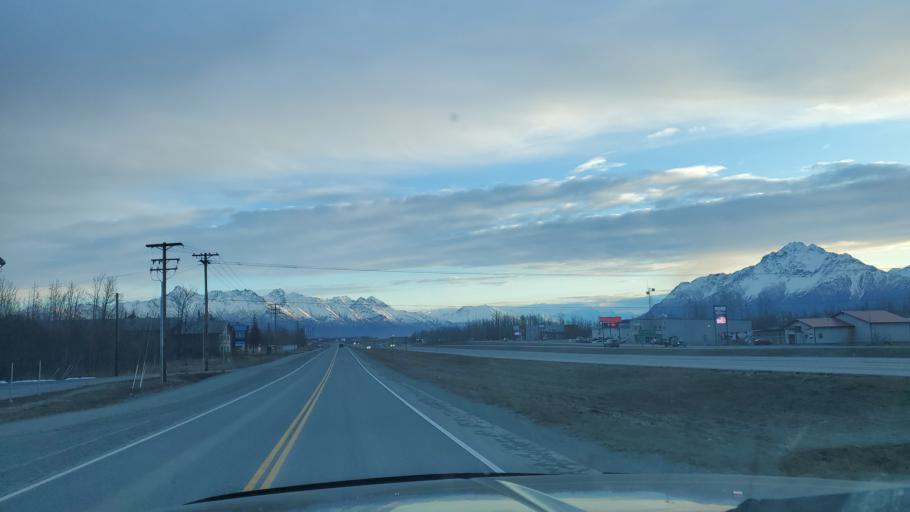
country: US
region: Alaska
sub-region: Matanuska-Susitna Borough
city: Lakes
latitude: 61.5632
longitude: -149.2935
